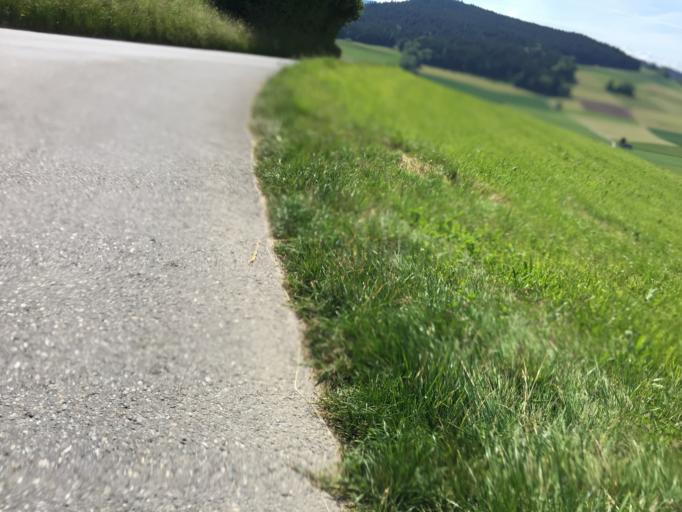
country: CH
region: Bern
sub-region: Bern-Mittelland District
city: Taegertschi
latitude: 46.8796
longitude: 7.5946
